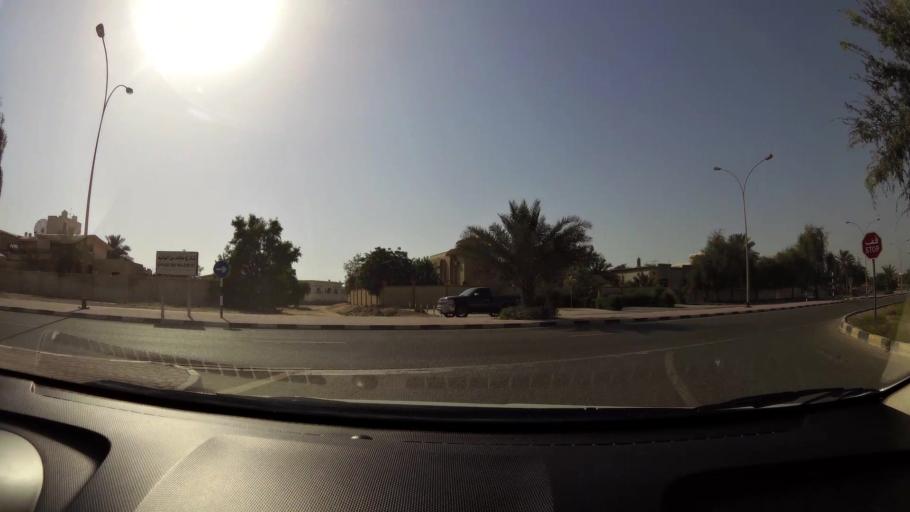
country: AE
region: Ajman
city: Ajman
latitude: 25.4062
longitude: 55.4645
